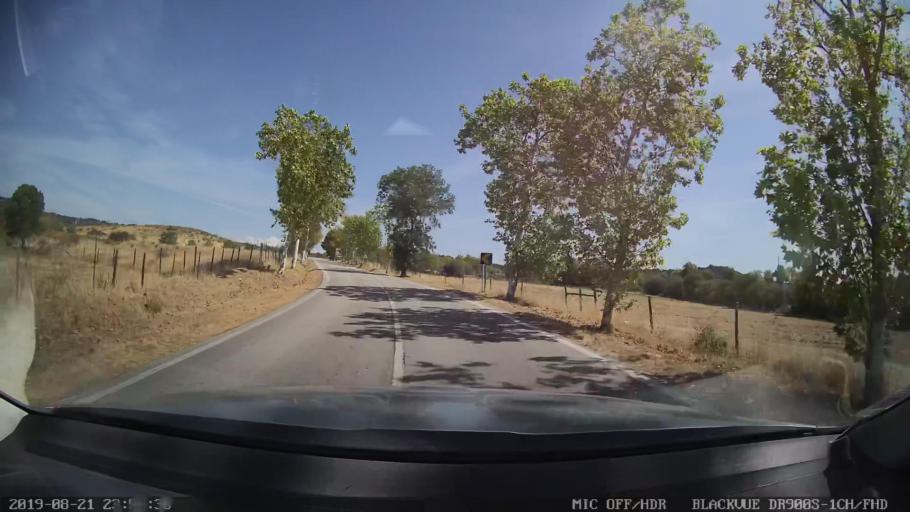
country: PT
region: Castelo Branco
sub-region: Idanha-A-Nova
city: Idanha-a-Nova
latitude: 39.9087
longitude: -7.2223
